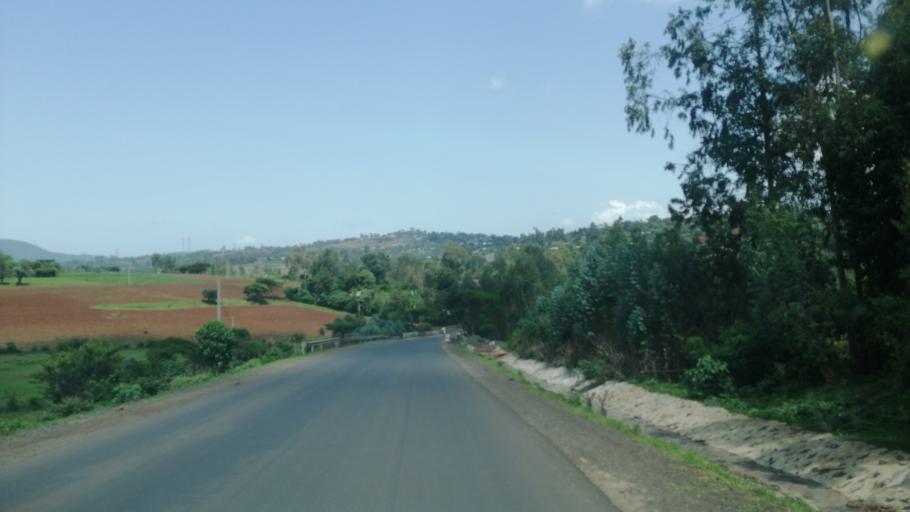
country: ET
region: Oromiya
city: Gedo
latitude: 8.9738
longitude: 37.5575
